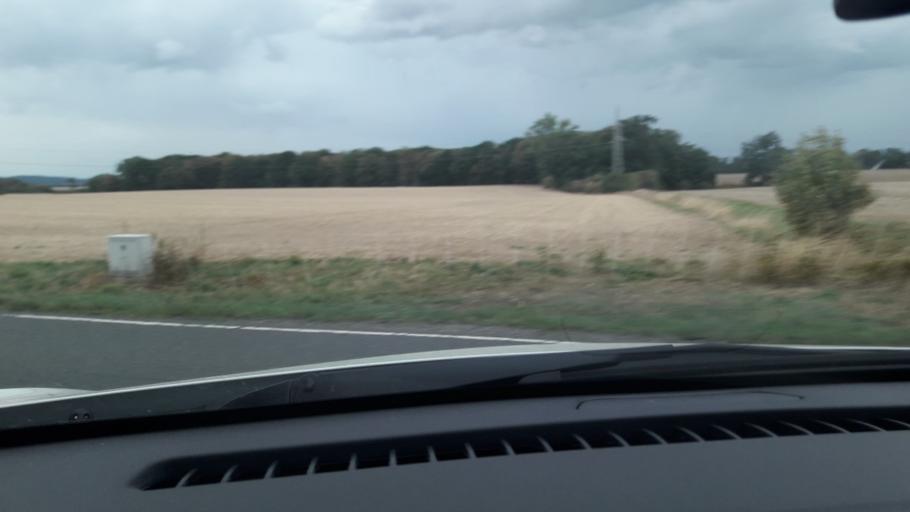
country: DE
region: Lower Saxony
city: Gielde
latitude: 52.0200
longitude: 10.4871
